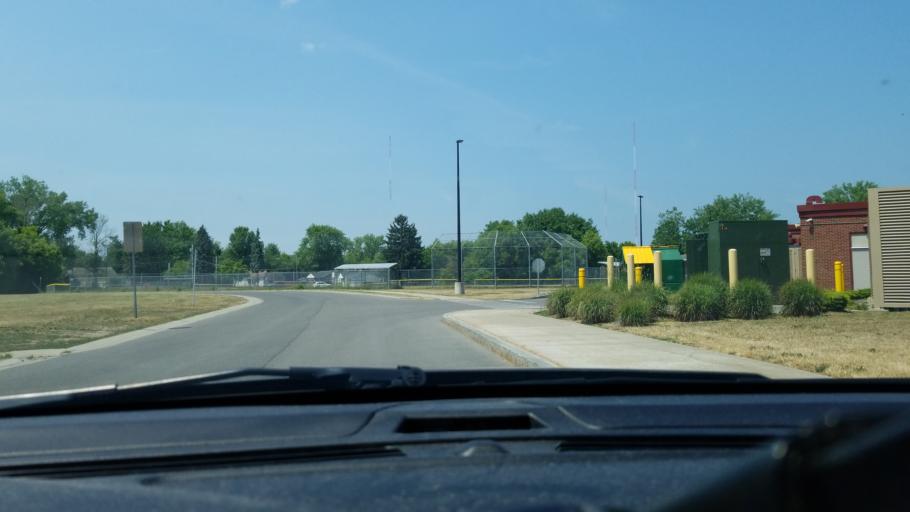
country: US
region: New York
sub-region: Onondaga County
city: Galeville
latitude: 43.0941
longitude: -76.1822
